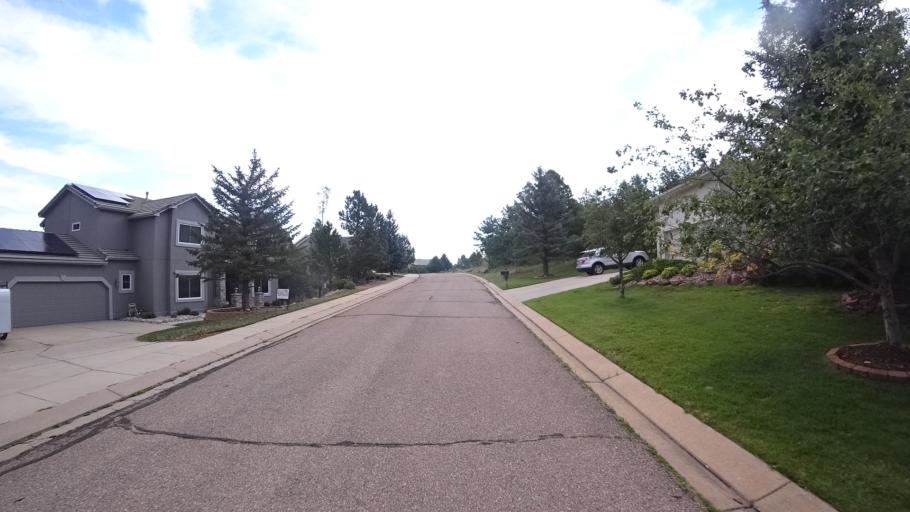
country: US
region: Colorado
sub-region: El Paso County
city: Air Force Academy
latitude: 38.9492
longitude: -104.8618
